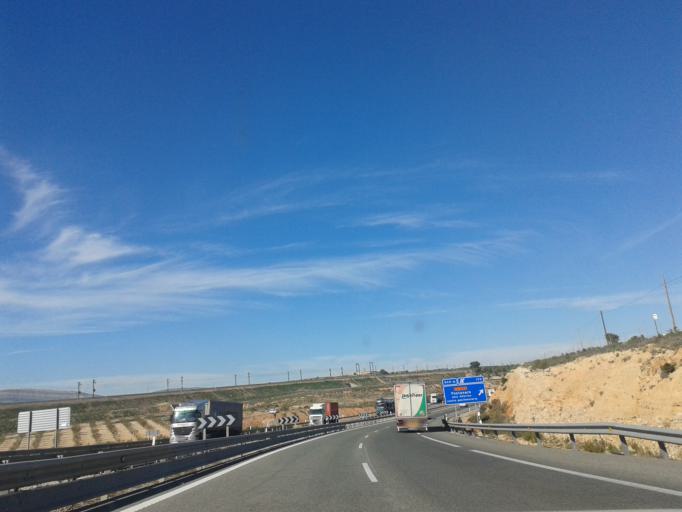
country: ES
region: Castille-La Mancha
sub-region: Provincia de Albacete
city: Caudete
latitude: 38.7065
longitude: -0.9270
